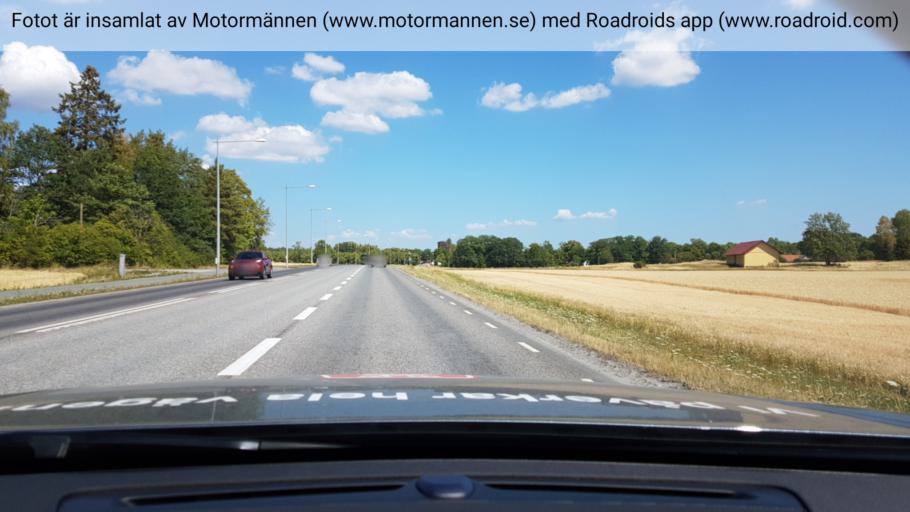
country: SE
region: Stockholm
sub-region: Ekero Kommun
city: Ekeroe
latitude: 59.3156
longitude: 17.8618
